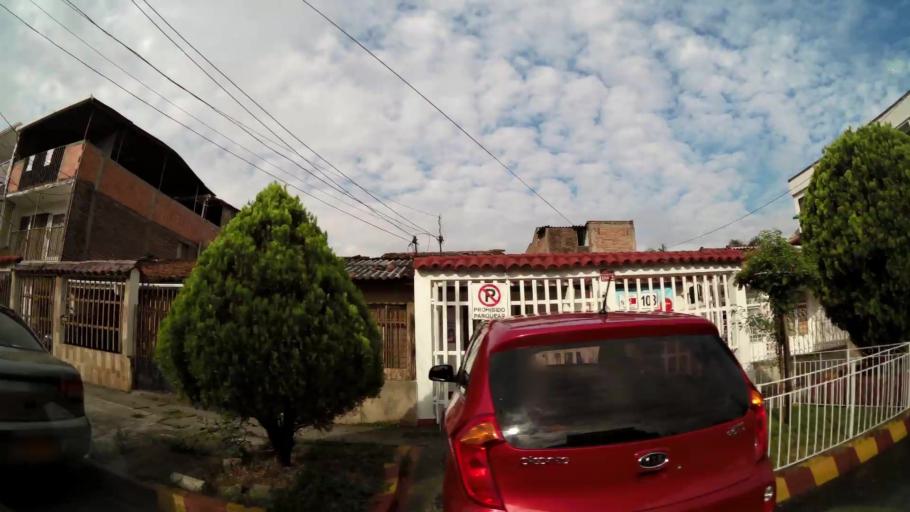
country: CO
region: Valle del Cauca
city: Cali
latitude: 3.4733
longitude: -76.4894
